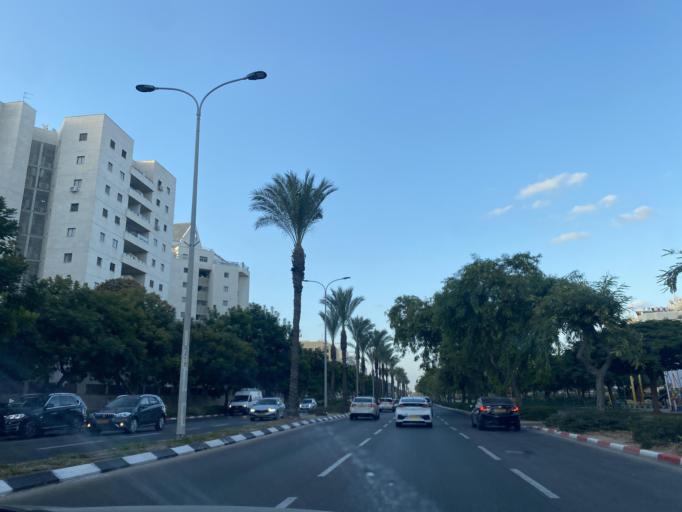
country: IL
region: Southern District
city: Ashdod
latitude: 31.7871
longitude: 34.6469
